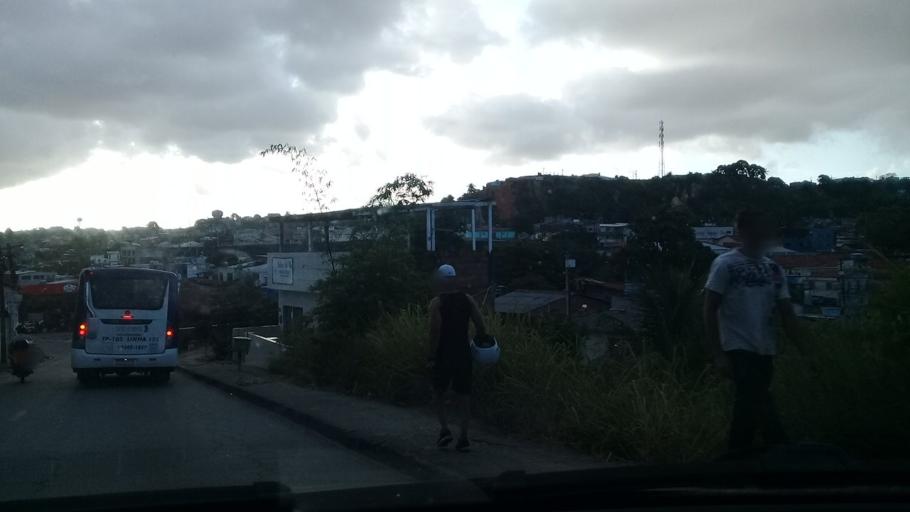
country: BR
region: Pernambuco
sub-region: Jaboatao Dos Guararapes
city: Jaboatao dos Guararapes
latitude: -8.1330
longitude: -34.9474
